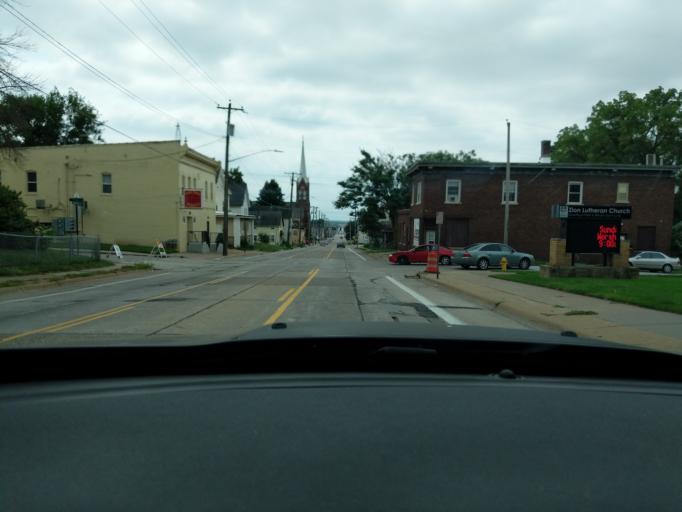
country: US
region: Iowa
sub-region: Scott County
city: Davenport
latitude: 41.5281
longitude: -90.5909
